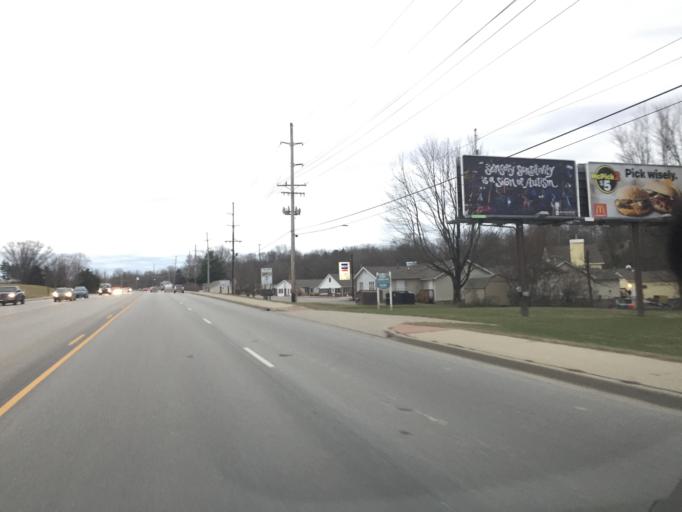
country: US
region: Indiana
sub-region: Monroe County
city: Ellettsville
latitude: 39.2192
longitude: -86.6025
